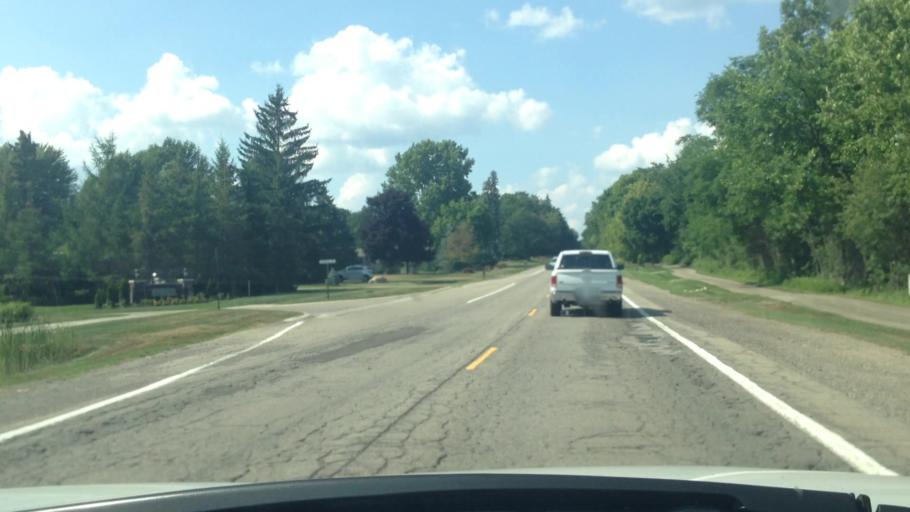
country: US
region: Michigan
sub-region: Oakland County
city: Clarkston
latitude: 42.7374
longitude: -83.3501
